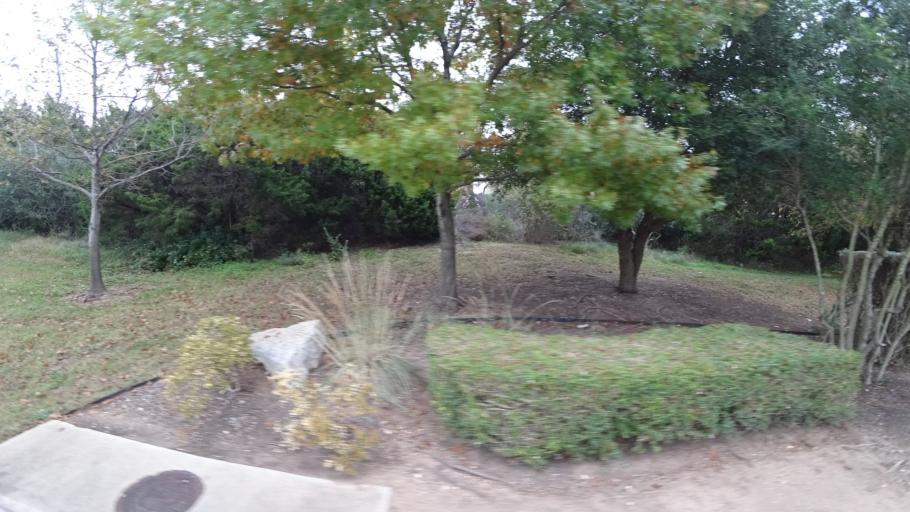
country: US
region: Texas
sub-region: Travis County
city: Bee Cave
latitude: 30.3584
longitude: -97.9092
